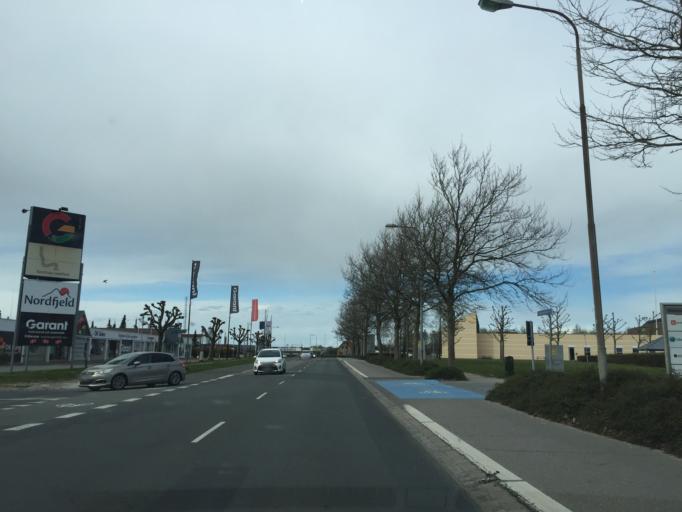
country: DK
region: South Denmark
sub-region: Odense Kommune
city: Neder Holluf
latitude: 55.3889
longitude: 10.4393
